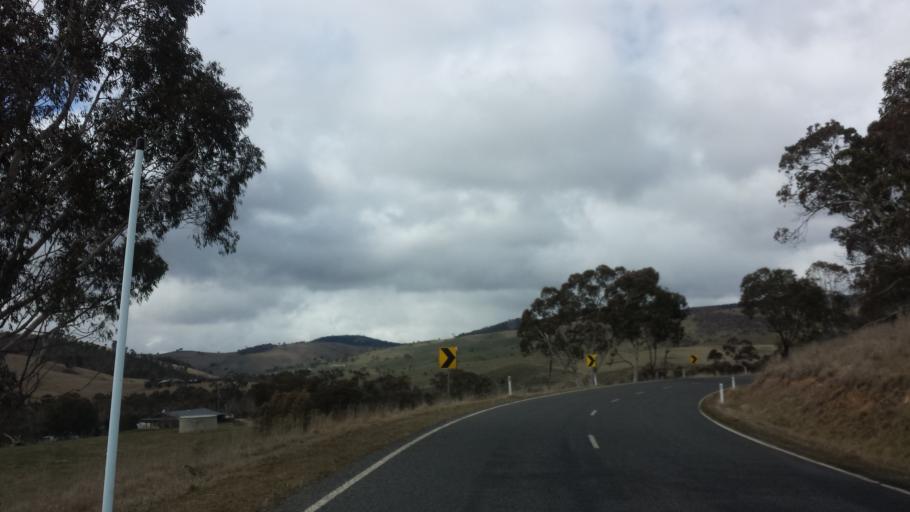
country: AU
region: Victoria
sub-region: Alpine
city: Mount Beauty
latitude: -37.0953
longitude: 147.4204
